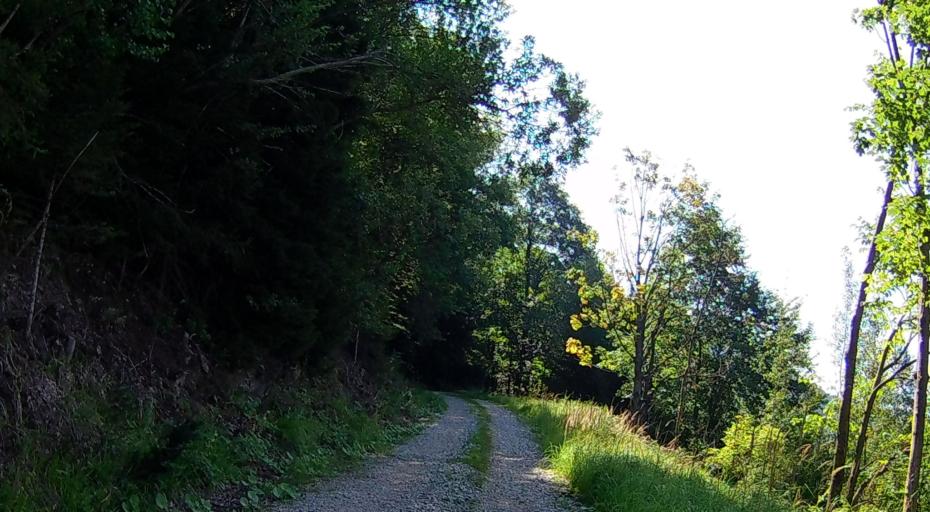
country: SI
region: Selnica ob Dravi
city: Selnica ob Dravi
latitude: 46.5055
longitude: 15.4662
